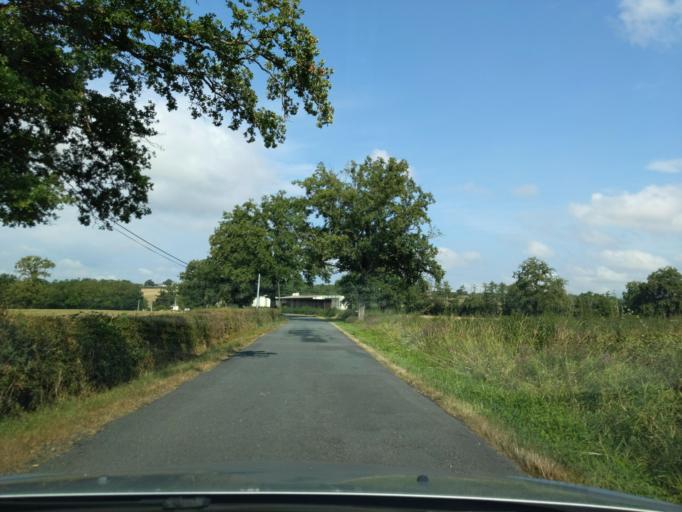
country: FR
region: Bourgogne
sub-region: Departement de Saone-et-Loire
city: Bourbon-Lancy
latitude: 46.6462
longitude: 3.7735
